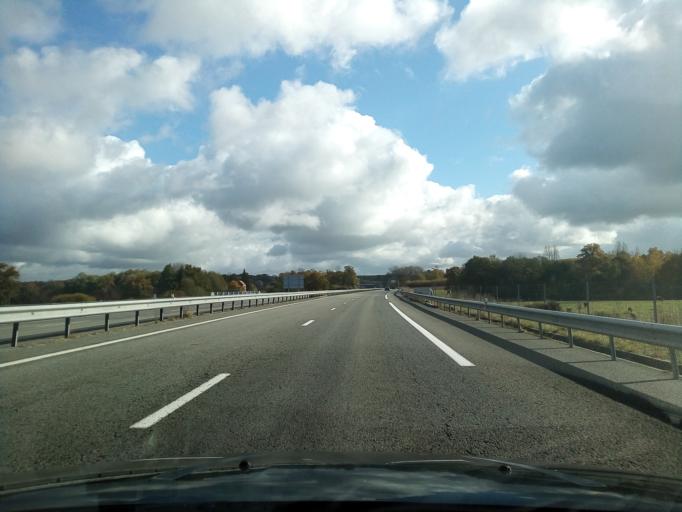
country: FR
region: Limousin
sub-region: Departement de la Creuse
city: Gouzon
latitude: 46.1985
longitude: 2.1395
